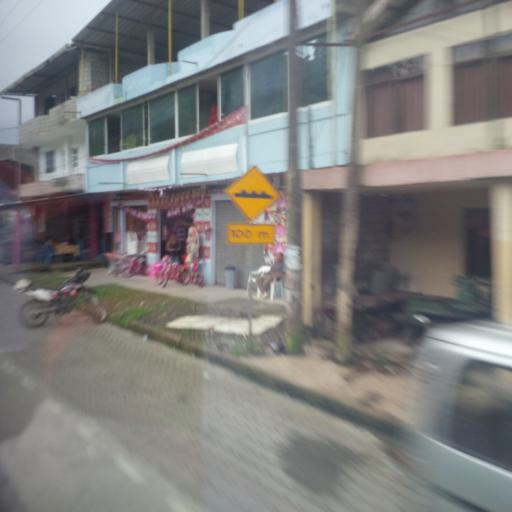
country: EC
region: Chimborazo
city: Alausi
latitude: -2.2004
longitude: -79.1213
